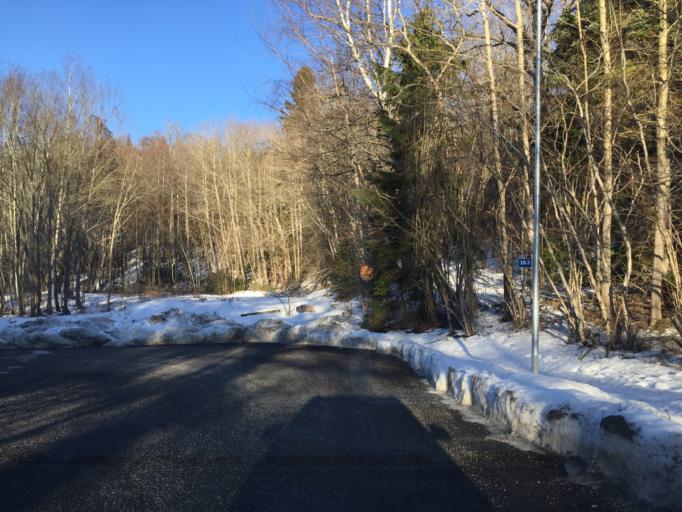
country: SE
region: Stockholm
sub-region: Salems Kommun
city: Ronninge
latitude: 59.1884
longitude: 17.7182
